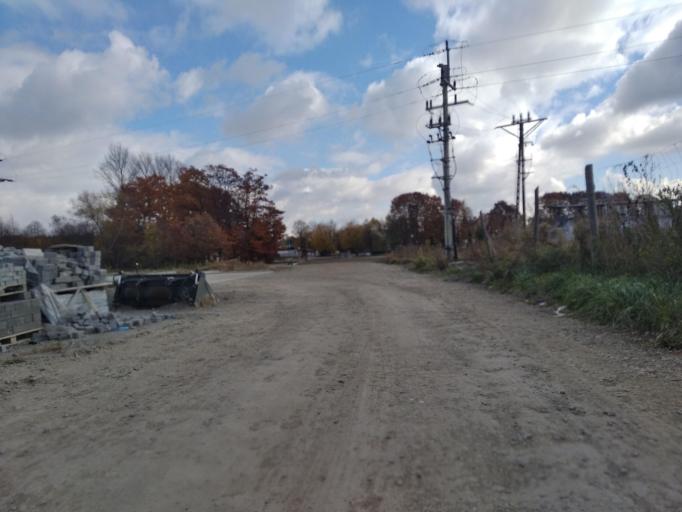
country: PL
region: Subcarpathian Voivodeship
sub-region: Powiat strzyzowski
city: Strzyzow
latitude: 49.8713
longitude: 21.7699
